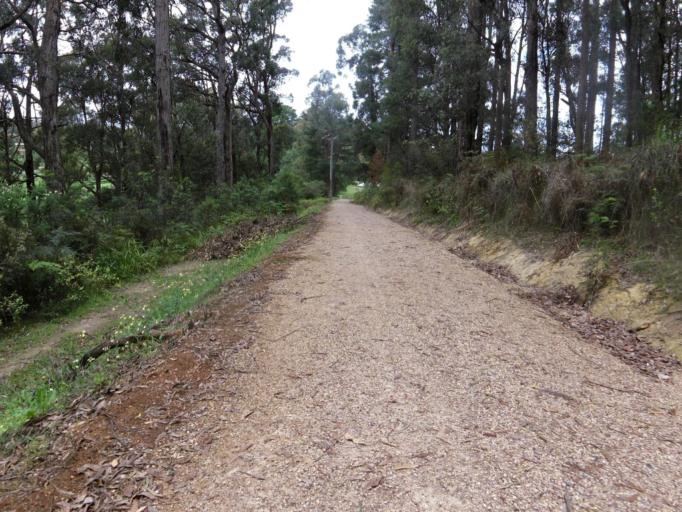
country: AU
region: Victoria
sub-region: Cardinia
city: Cockatoo
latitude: -37.9446
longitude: 145.5032
